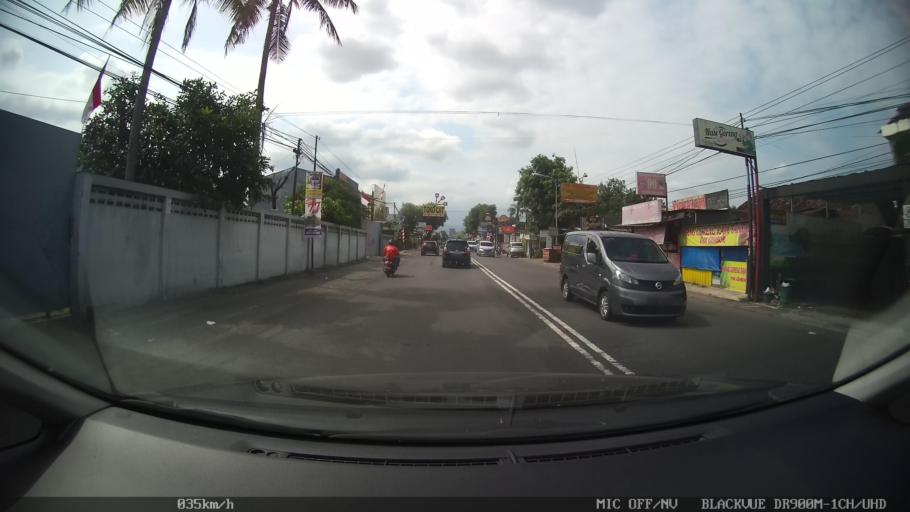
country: ID
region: Daerah Istimewa Yogyakarta
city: Depok
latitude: -7.7546
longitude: 110.4339
